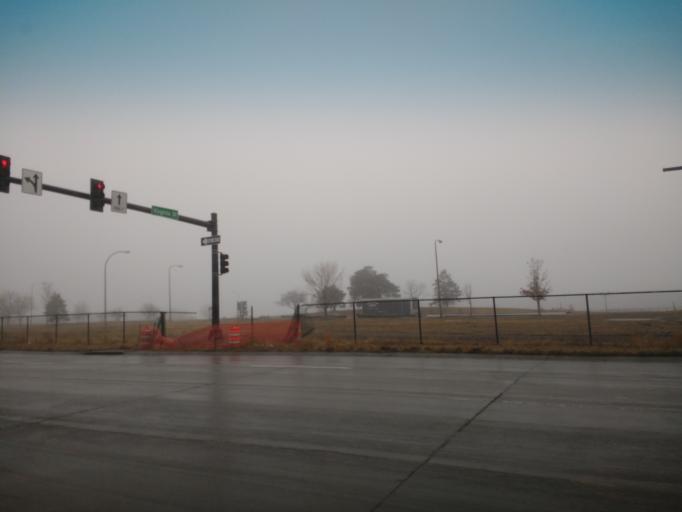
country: US
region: Iowa
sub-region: Woodbury County
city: Sioux City
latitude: 42.4879
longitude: -96.3984
